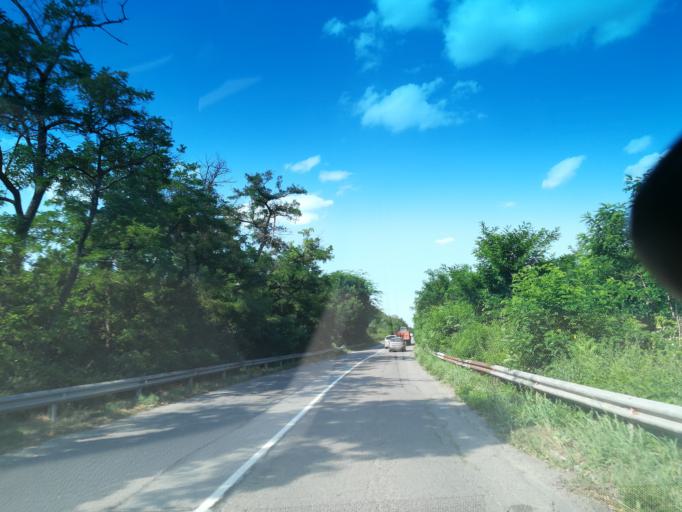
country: BG
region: Stara Zagora
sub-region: Obshtina Chirpan
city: Chirpan
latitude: 42.2371
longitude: 25.3983
